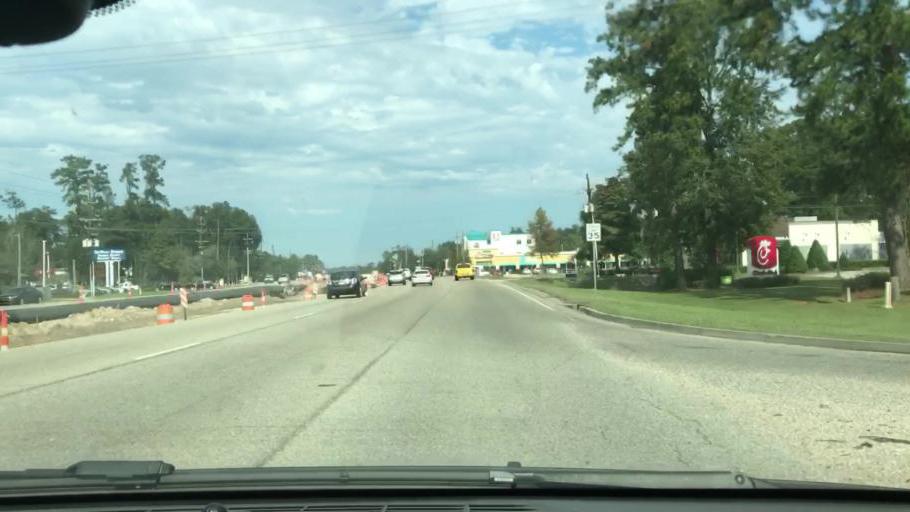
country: US
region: Louisiana
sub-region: Saint Tammany Parish
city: Covington
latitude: 30.4445
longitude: -90.0821
